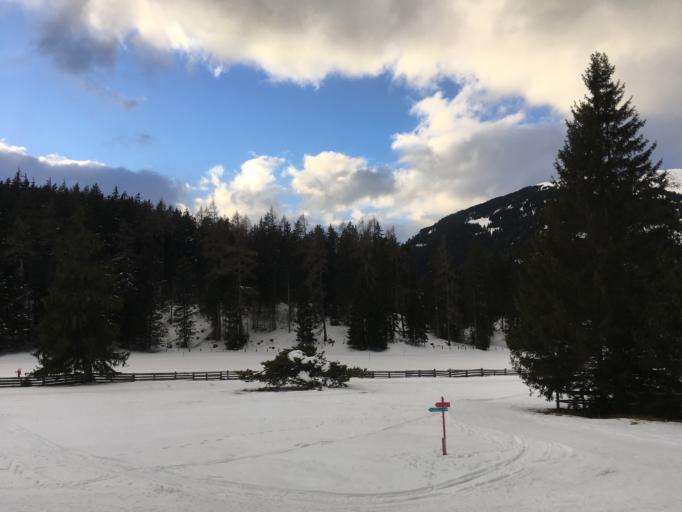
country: CH
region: Grisons
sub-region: Albula District
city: Tiefencastel
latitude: 46.6988
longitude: 9.5579
